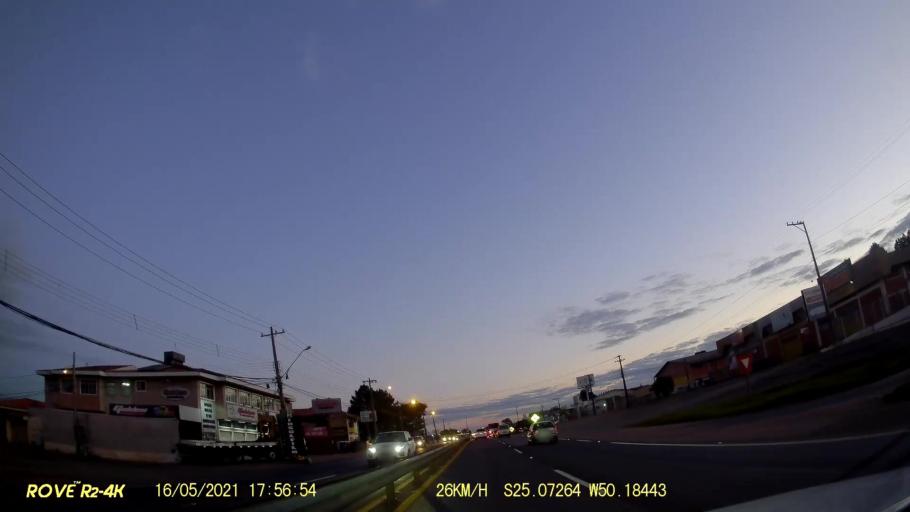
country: BR
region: Parana
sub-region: Ponta Grossa
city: Ponta Grossa
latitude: -25.0727
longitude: -50.1844
